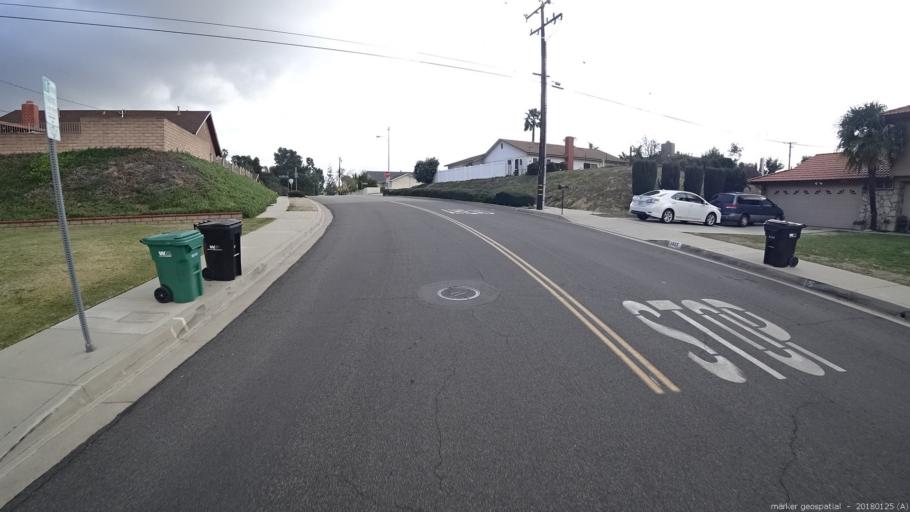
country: US
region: California
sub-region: Los Angeles County
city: Walnut
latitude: 33.9864
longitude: -117.8412
